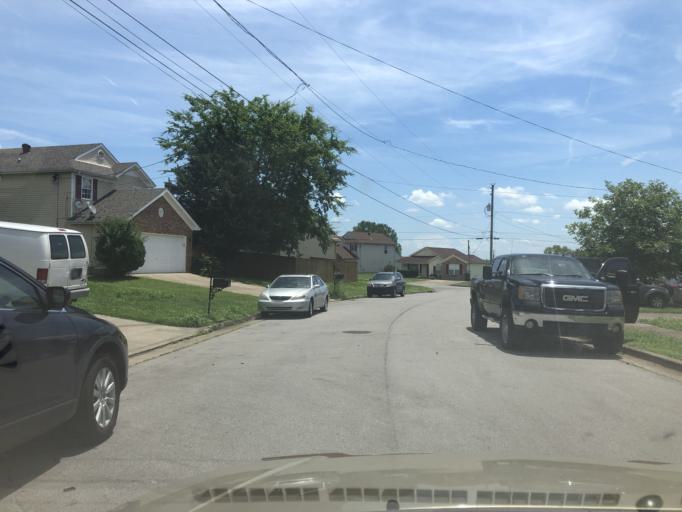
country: US
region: Tennessee
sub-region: Davidson County
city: Lakewood
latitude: 36.2540
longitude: -86.6752
